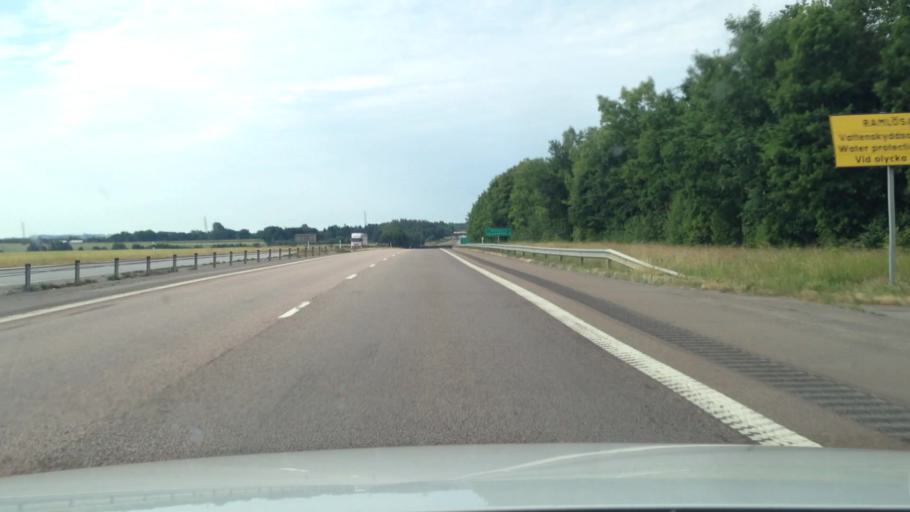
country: SE
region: Skane
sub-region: Helsingborg
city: Barslov
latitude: 56.0295
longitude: 12.7851
